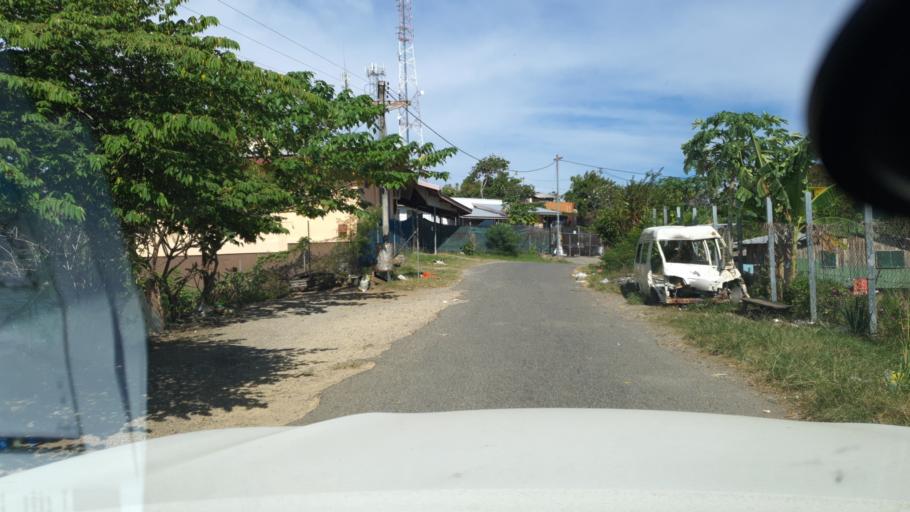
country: SB
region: Guadalcanal
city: Honiara
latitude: -9.4382
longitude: 159.9521
